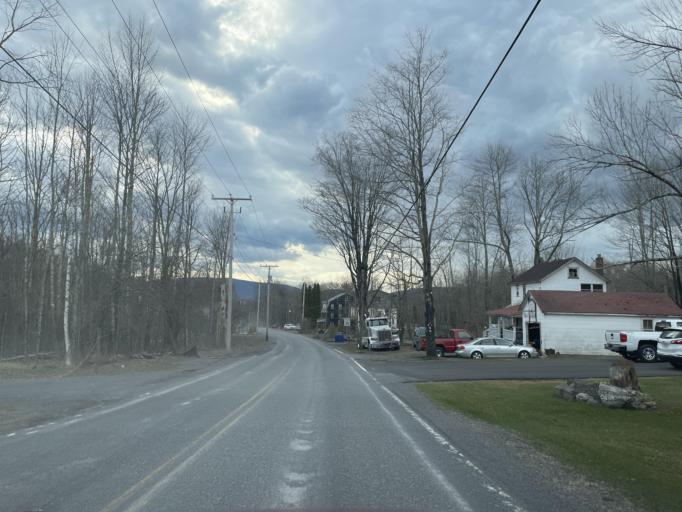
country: US
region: New York
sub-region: Greene County
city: Palenville
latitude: 42.1991
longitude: -74.0841
